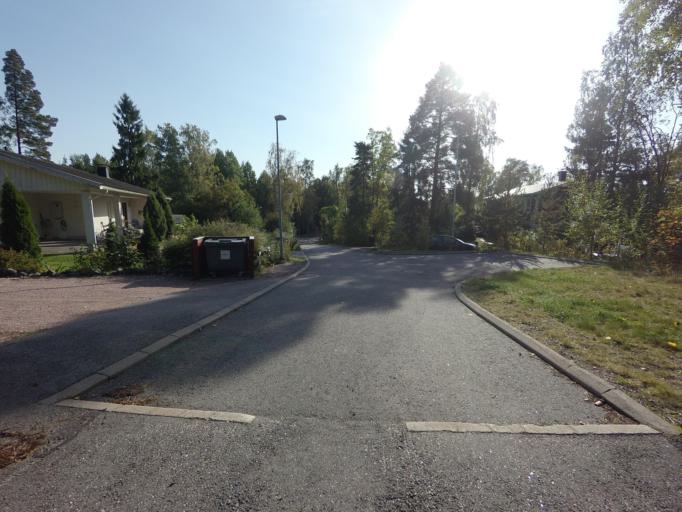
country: FI
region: Uusimaa
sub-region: Helsinki
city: Espoo
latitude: 60.1709
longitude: 24.6389
